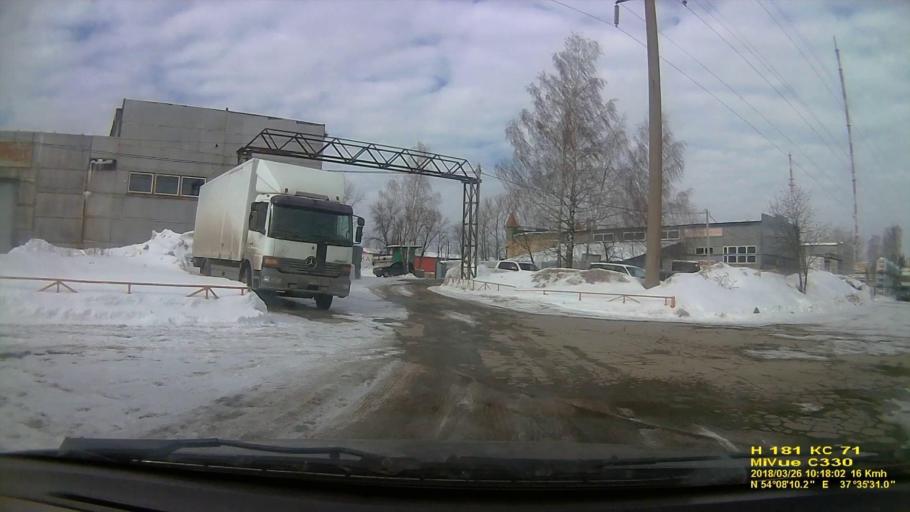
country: RU
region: Tula
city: Mendeleyevskiy
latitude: 54.1357
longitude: 37.5948
